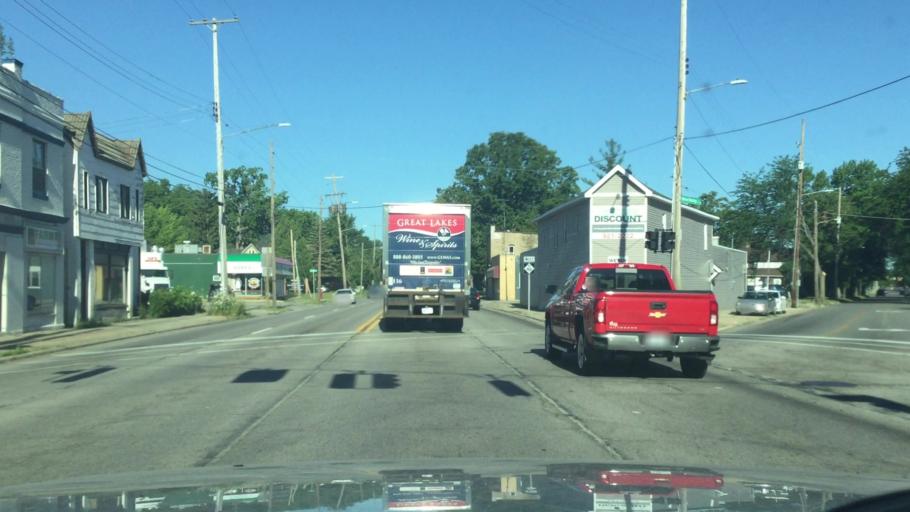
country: US
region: Michigan
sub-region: Saginaw County
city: Saginaw
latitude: 43.4150
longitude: -83.9755
